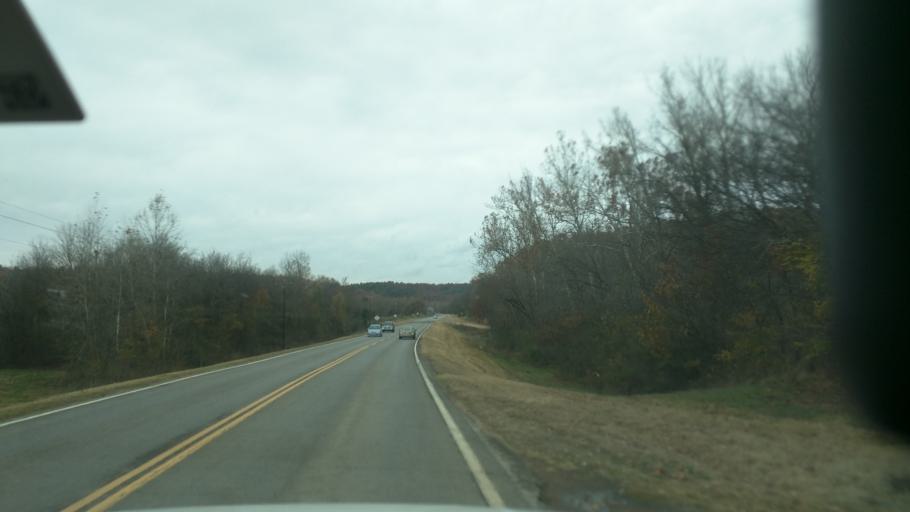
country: US
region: Oklahoma
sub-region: Cherokee County
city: Park Hill
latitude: 35.9122
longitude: -94.8334
